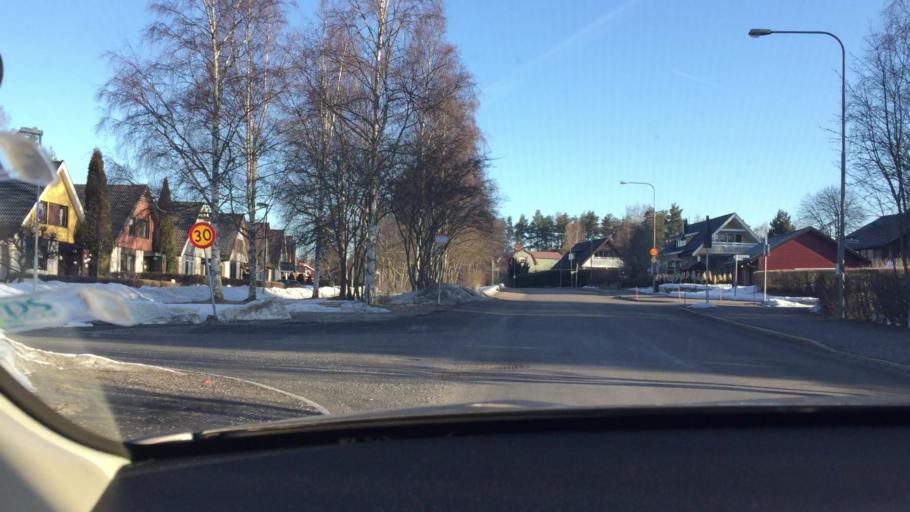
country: SE
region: Dalarna
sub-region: Faluns Kommun
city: Falun
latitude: 60.5720
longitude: 15.6510
